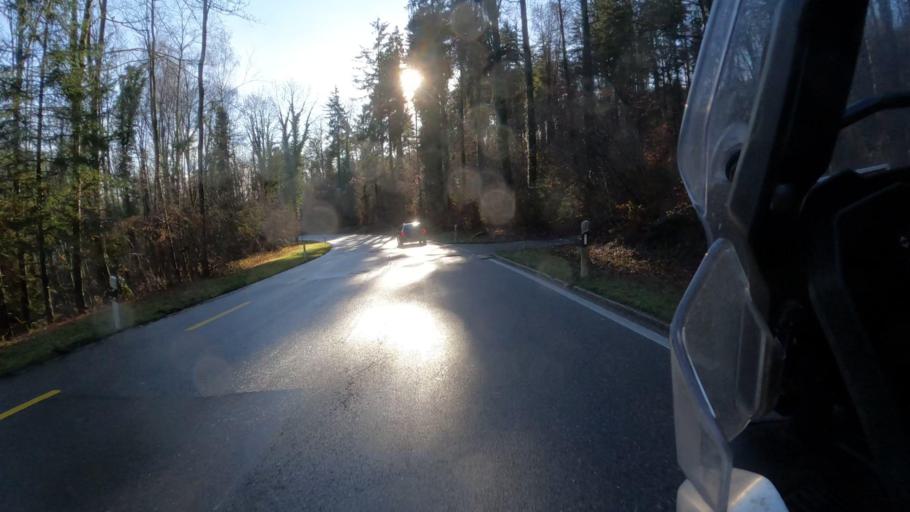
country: CH
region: Zurich
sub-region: Bezirk Buelach
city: Rorbas
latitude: 47.5179
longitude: 8.5782
